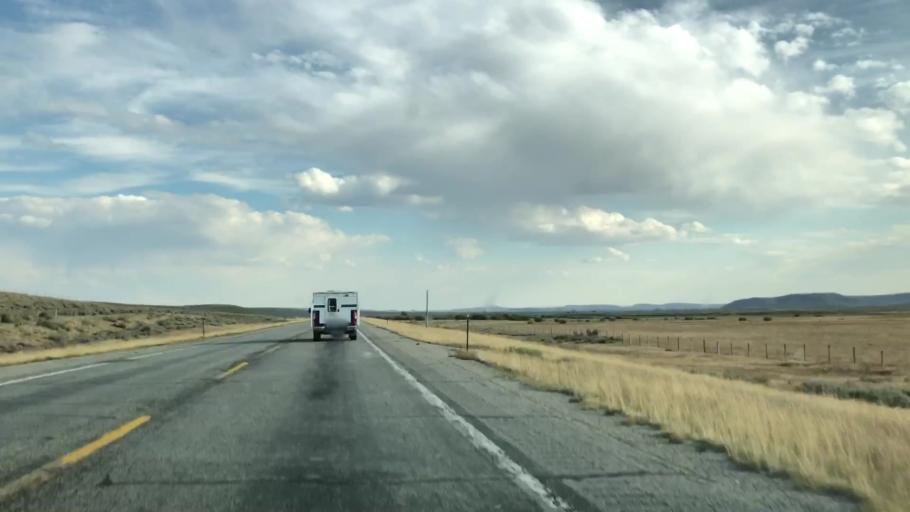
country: US
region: Wyoming
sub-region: Sublette County
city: Pinedale
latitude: 43.0294
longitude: -110.1267
